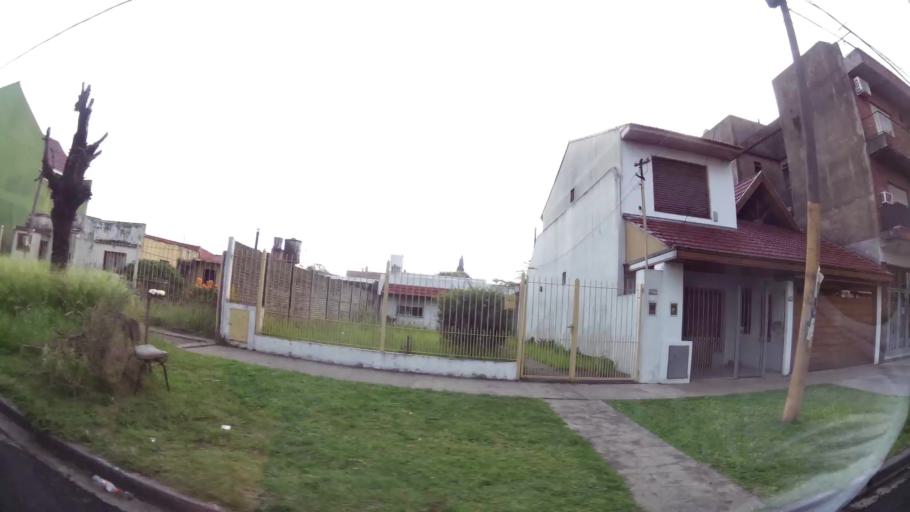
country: AR
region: Buenos Aires
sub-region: Partido de Quilmes
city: Quilmes
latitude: -34.7377
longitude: -58.2543
